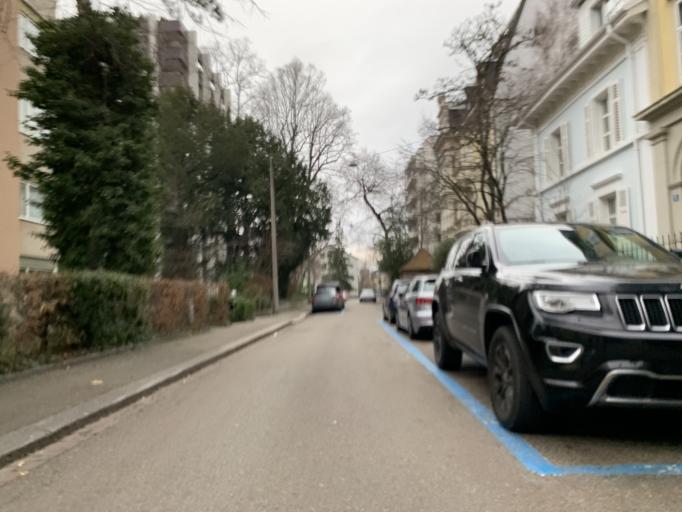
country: CH
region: Basel-Landschaft
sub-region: Bezirk Arlesheim
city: Birsfelden
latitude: 47.5512
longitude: 7.6072
